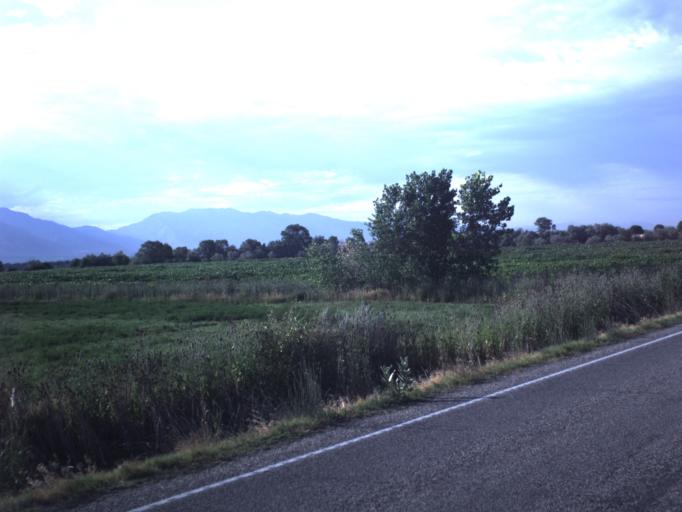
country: US
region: Utah
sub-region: Weber County
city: Plain City
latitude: 41.2728
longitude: -112.0923
